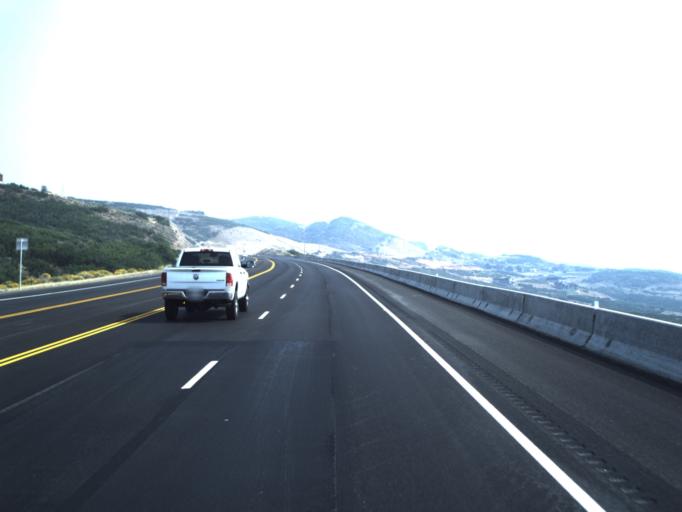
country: US
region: Utah
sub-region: Summit County
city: Park City
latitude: 40.6543
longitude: -111.4105
